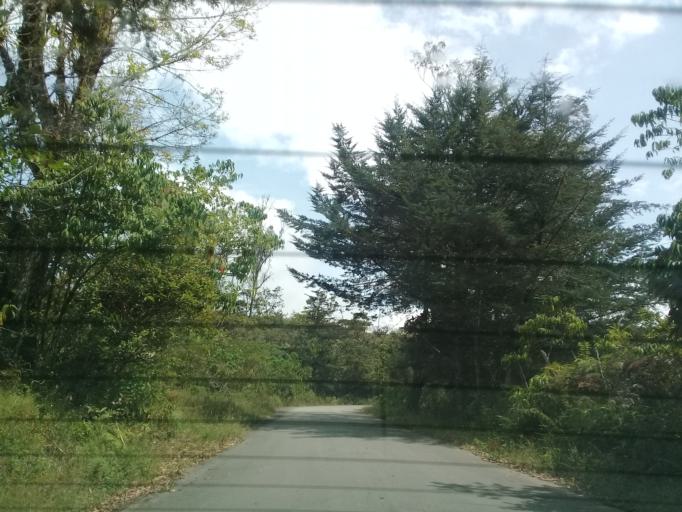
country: CO
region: Cundinamarca
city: Gachala
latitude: 4.6995
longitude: -73.4883
